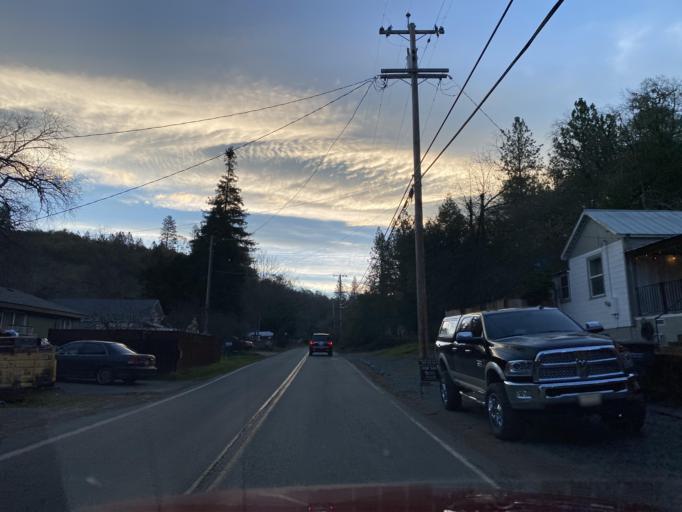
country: US
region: California
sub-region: Amador County
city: Plymouth
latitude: 38.5036
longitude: -120.7556
